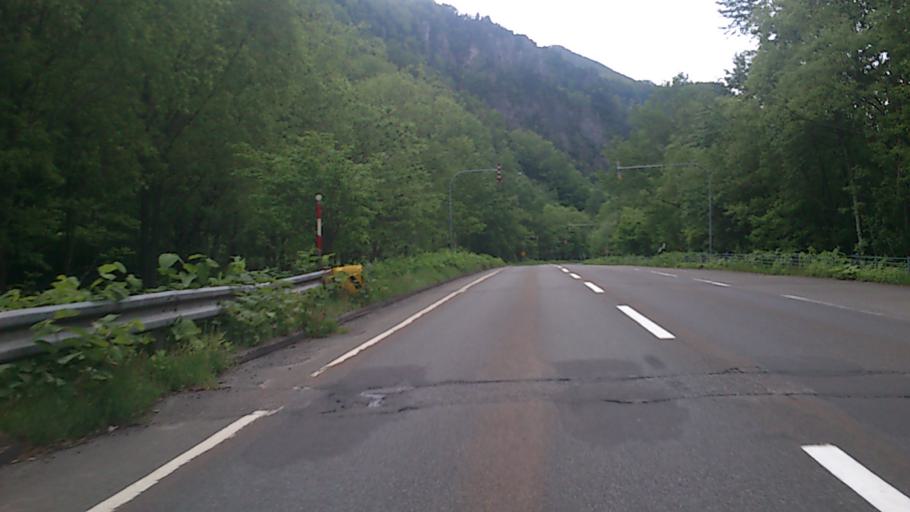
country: JP
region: Hokkaido
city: Kamikawa
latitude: 43.7540
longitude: 142.9288
